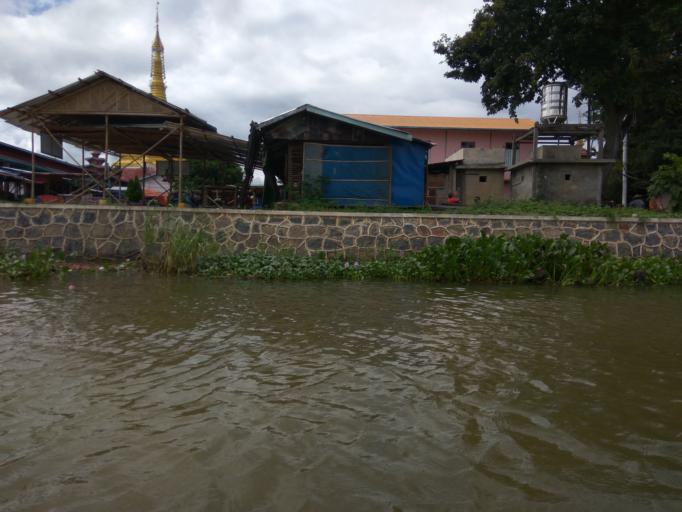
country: MM
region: Shan
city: Taunggyi
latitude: 20.4598
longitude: 96.9053
